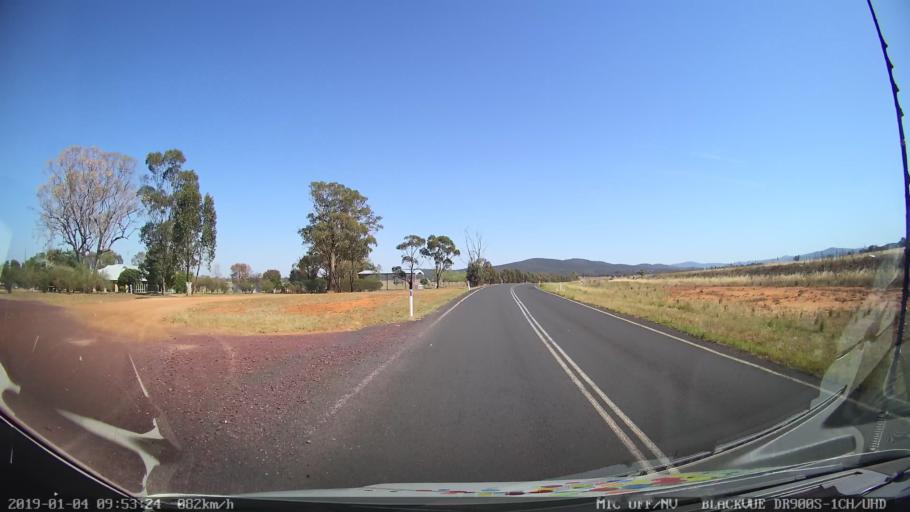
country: AU
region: New South Wales
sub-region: Cabonne
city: Canowindra
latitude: -33.5533
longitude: 148.4201
